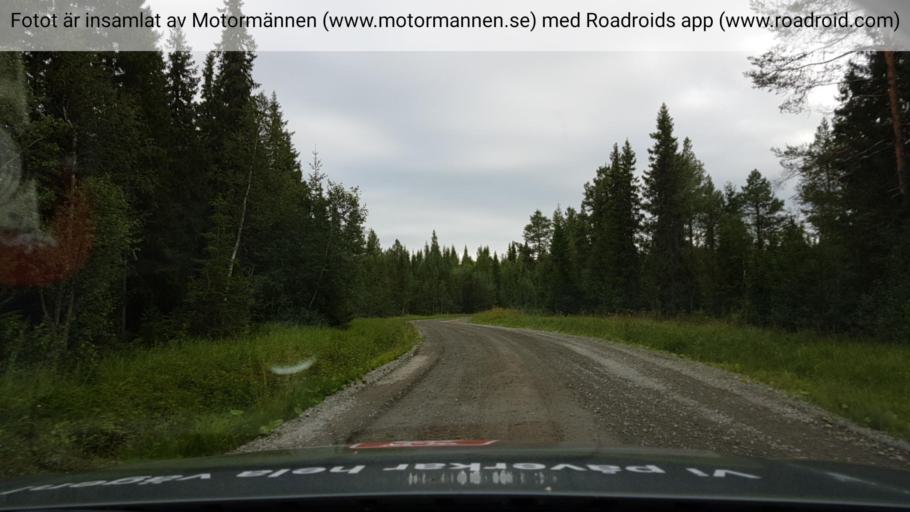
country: SE
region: Jaemtland
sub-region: Krokoms Kommun
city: Valla
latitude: 63.4001
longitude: 14.0742
